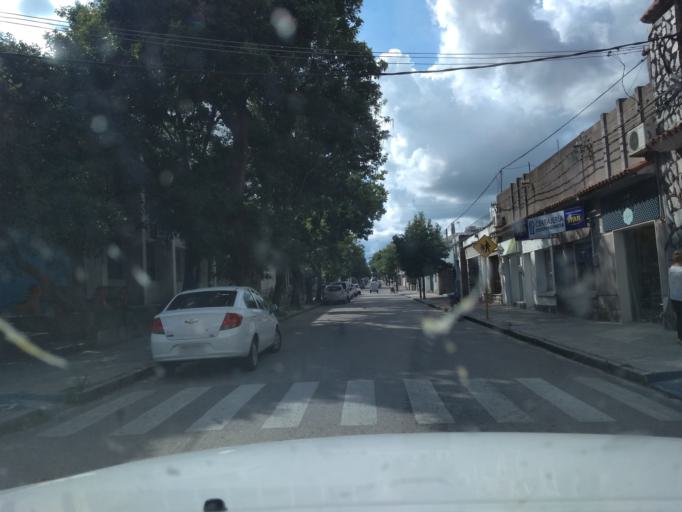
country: UY
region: Florida
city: Florida
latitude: -34.0984
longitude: -56.2141
